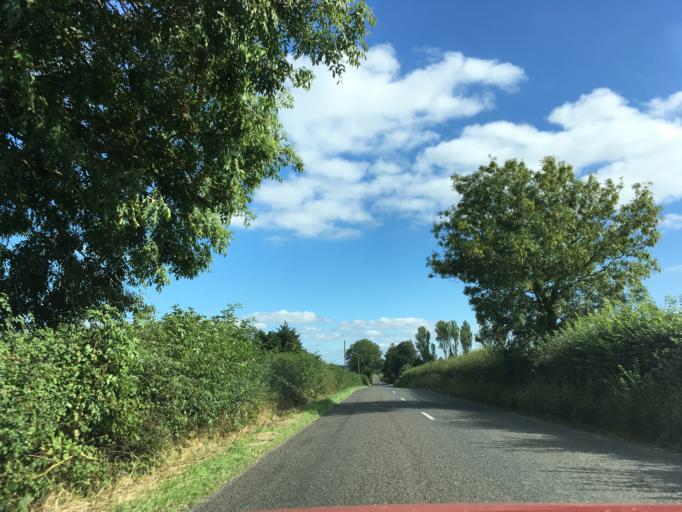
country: IE
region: Munster
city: Cashel
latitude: 52.4736
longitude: -7.9242
